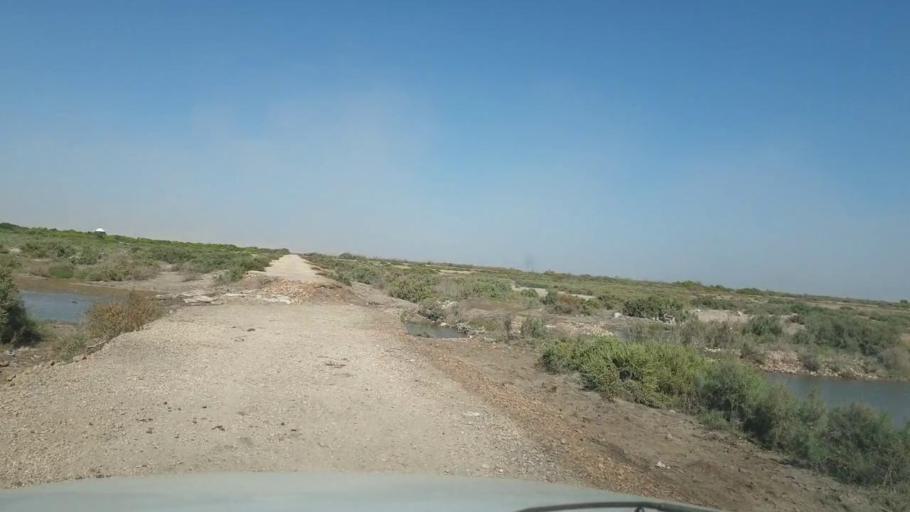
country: PK
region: Sindh
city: Mirpur Sakro
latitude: 24.4633
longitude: 67.6919
